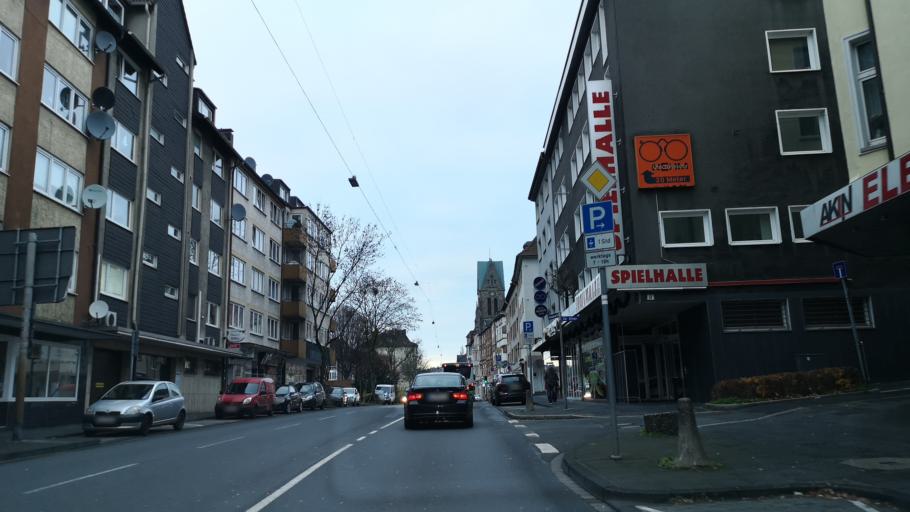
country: DE
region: North Rhine-Westphalia
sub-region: Regierungsbezirk Arnsberg
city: Hagen
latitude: 51.3658
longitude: 7.4632
